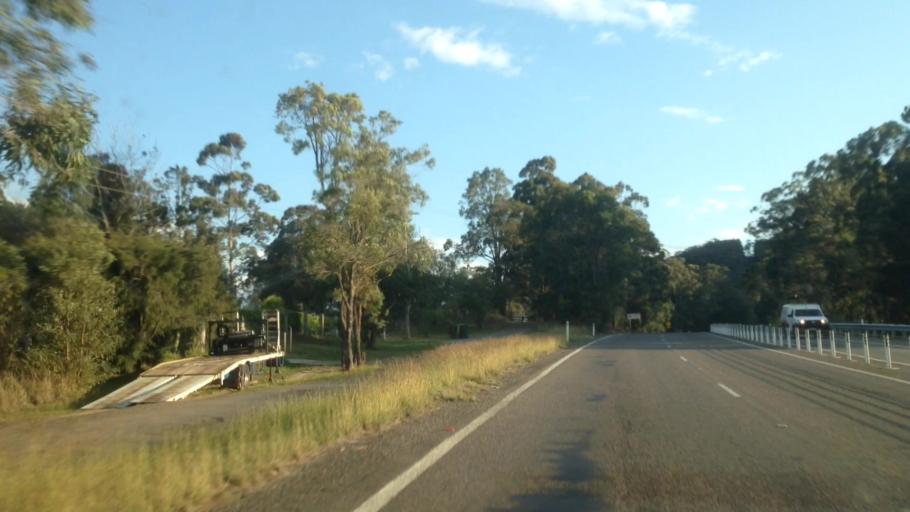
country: AU
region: New South Wales
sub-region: Lake Macquarie Shire
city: Cooranbong
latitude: -32.9580
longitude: 151.4809
